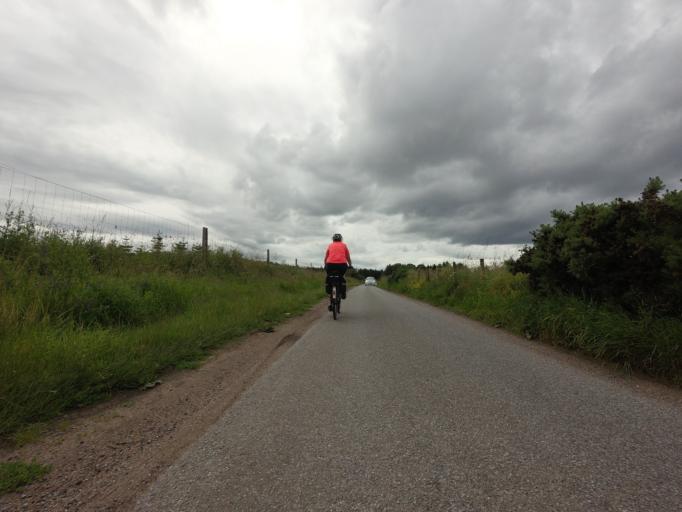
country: GB
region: Scotland
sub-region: Highland
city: Nairn
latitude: 57.6017
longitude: -3.7771
